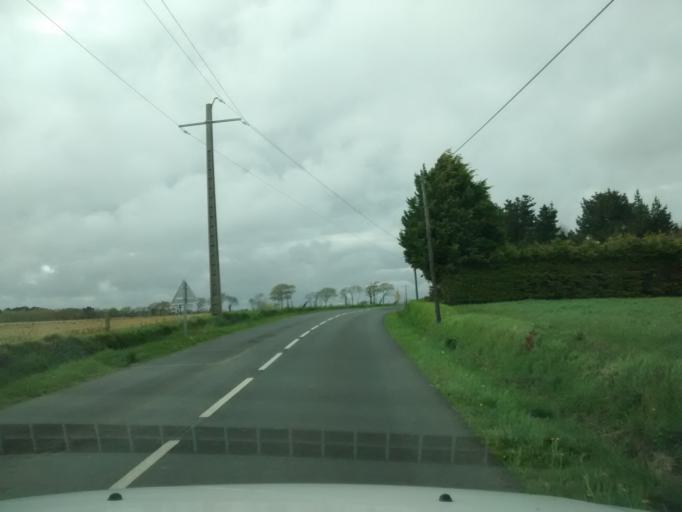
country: FR
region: Brittany
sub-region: Departement du Finistere
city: Clohars-Carnoet
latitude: 47.7962
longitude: -3.5534
